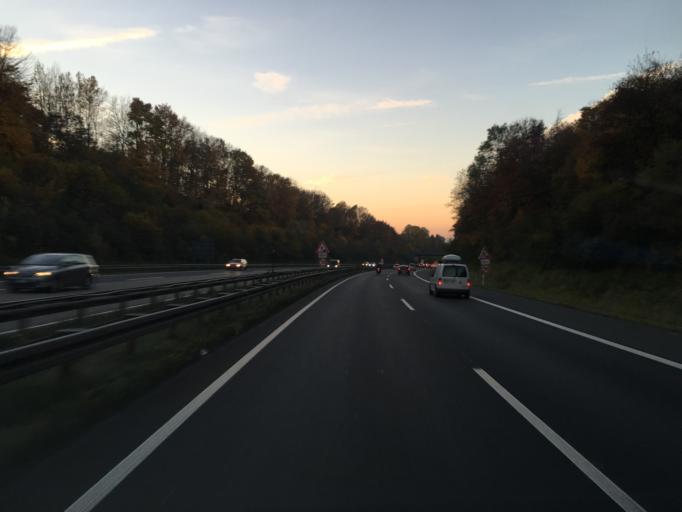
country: DE
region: North Rhine-Westphalia
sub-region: Regierungsbezirk Arnsberg
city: Schalksmuhle
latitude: 51.2902
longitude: 7.5598
